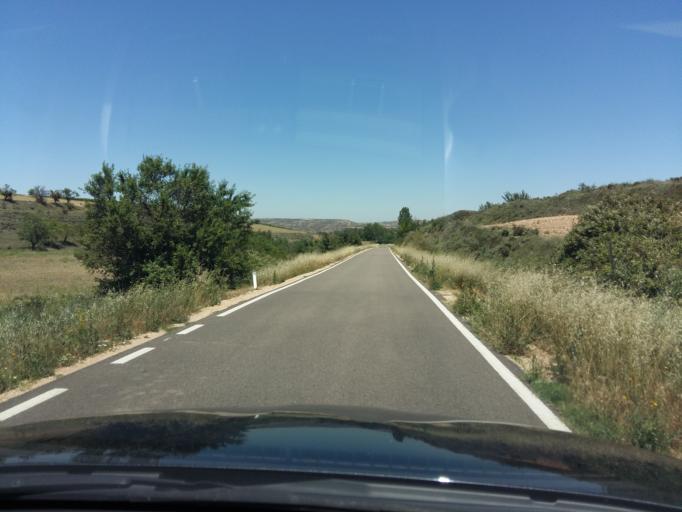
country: ES
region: Aragon
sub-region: Provincia de Zaragoza
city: Alcala de Moncayo
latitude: 41.7974
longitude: -1.6965
